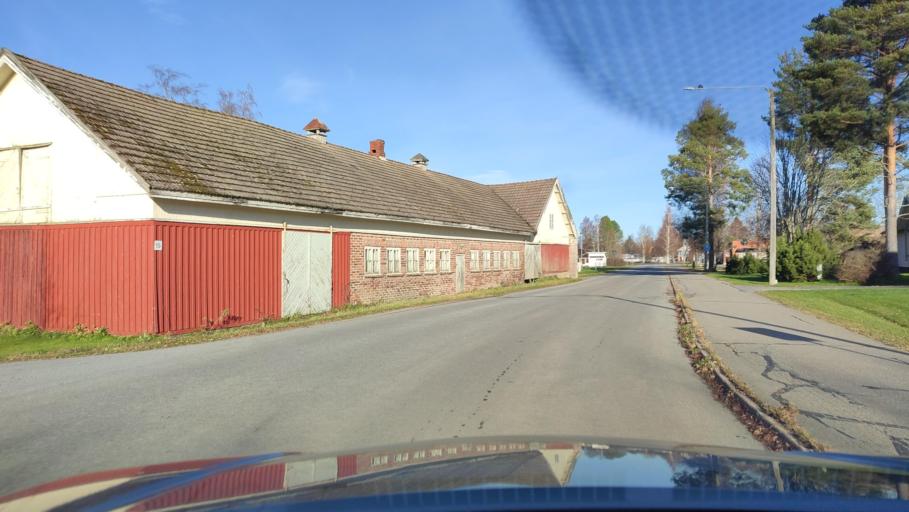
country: FI
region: Southern Ostrobothnia
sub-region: Suupohja
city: Teuva
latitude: 62.4832
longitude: 21.7499
